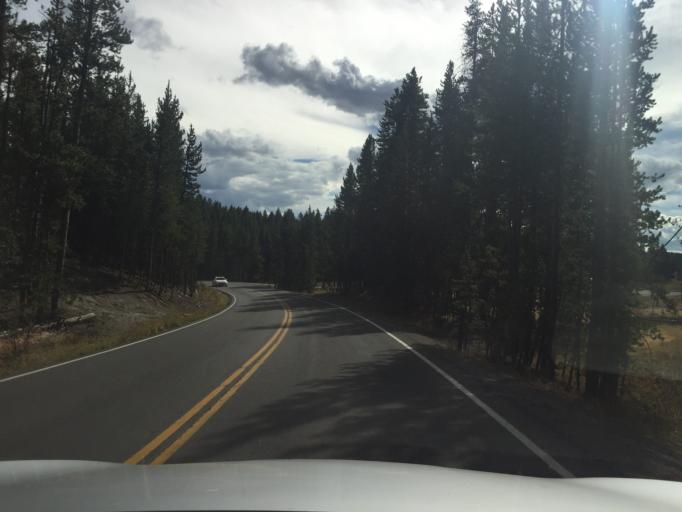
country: US
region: Montana
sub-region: Gallatin County
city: West Yellowstone
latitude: 44.7109
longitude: -110.5053
